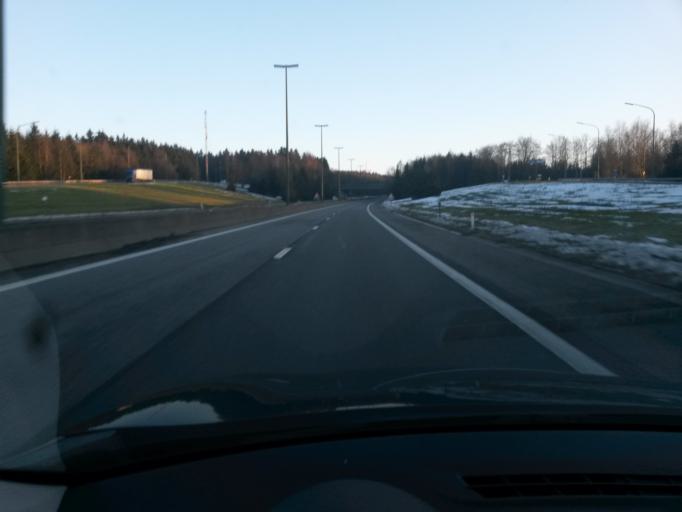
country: BE
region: Wallonia
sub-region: Province de Liege
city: Saint-Vith
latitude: 50.3409
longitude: 6.0872
